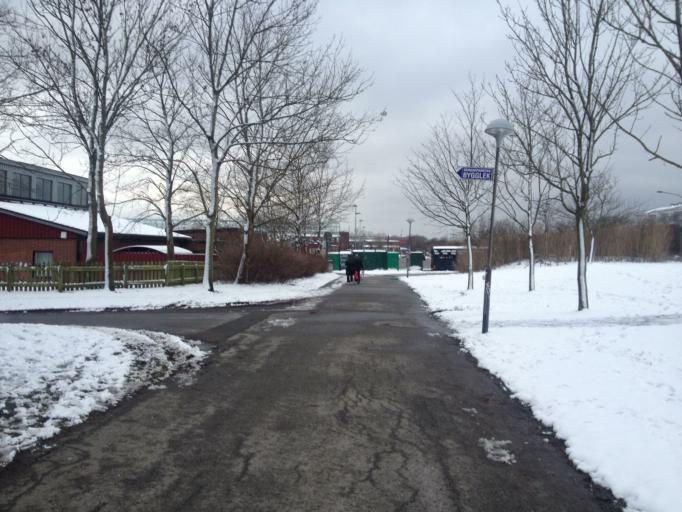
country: SE
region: Skane
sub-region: Lunds Kommun
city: Lund
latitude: 55.7241
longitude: 13.2060
